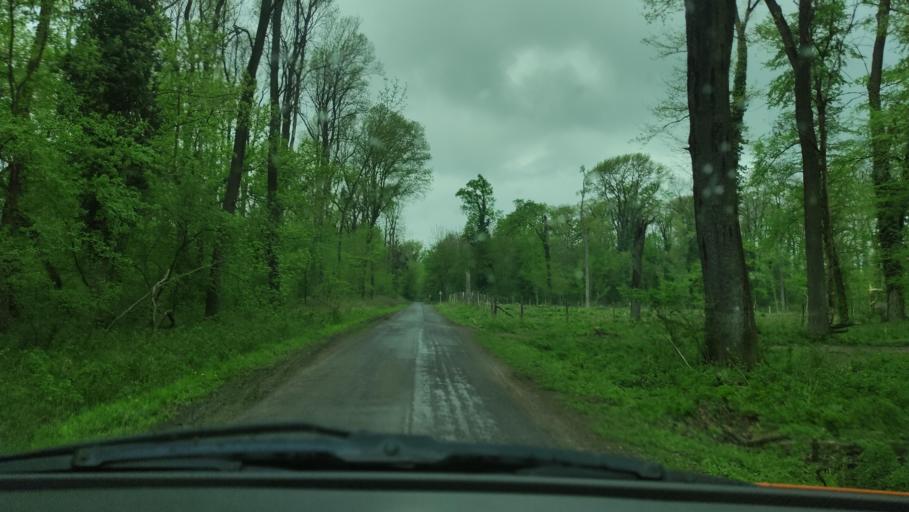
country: HU
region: Baranya
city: Mohacs
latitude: 45.9100
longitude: 18.7345
